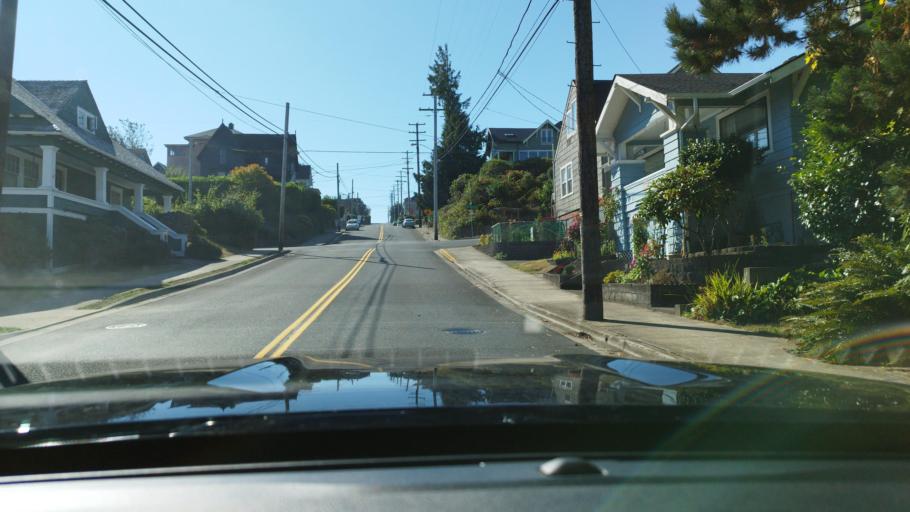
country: US
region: Oregon
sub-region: Clatsop County
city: Astoria
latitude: 46.1861
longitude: -123.8348
